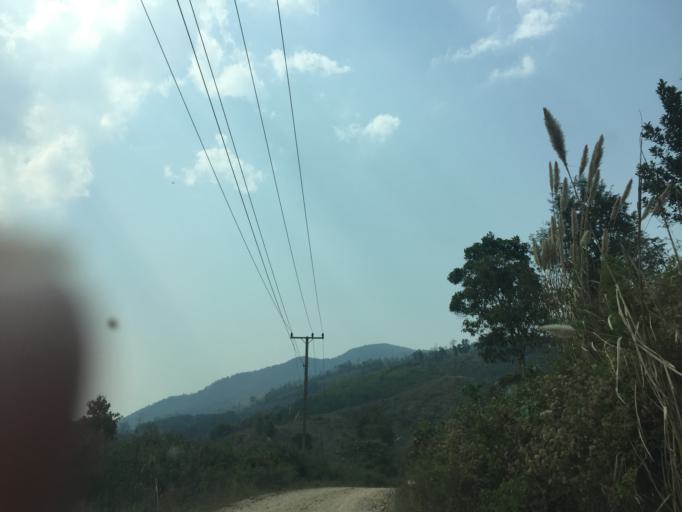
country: TH
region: Nan
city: Song Khwae
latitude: 19.7381
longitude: 100.7176
